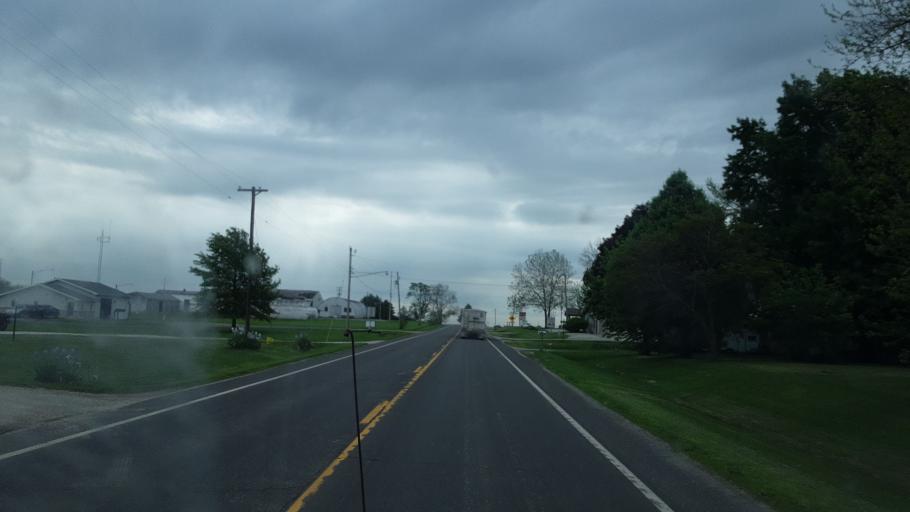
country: US
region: Illinois
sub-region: Fulton County
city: Astoria
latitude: 40.3514
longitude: -90.3181
